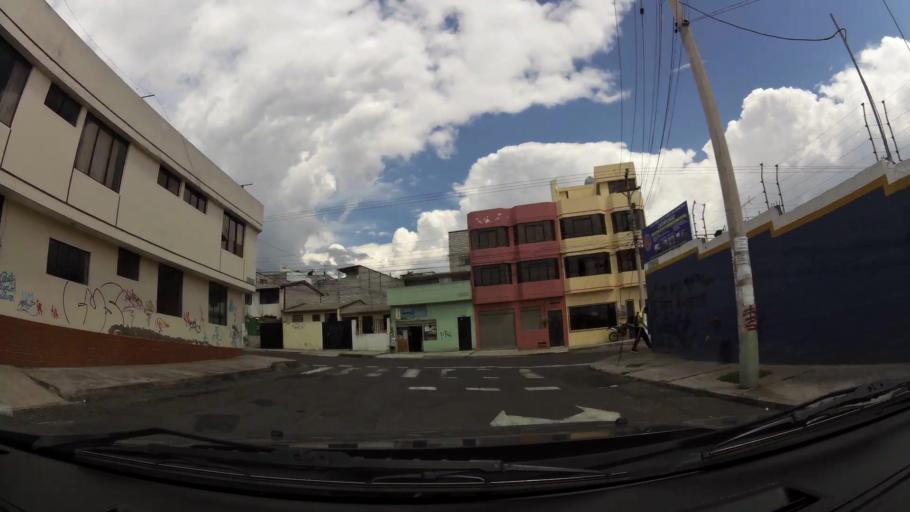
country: EC
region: Pichincha
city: Quito
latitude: -0.0920
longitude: -78.4542
